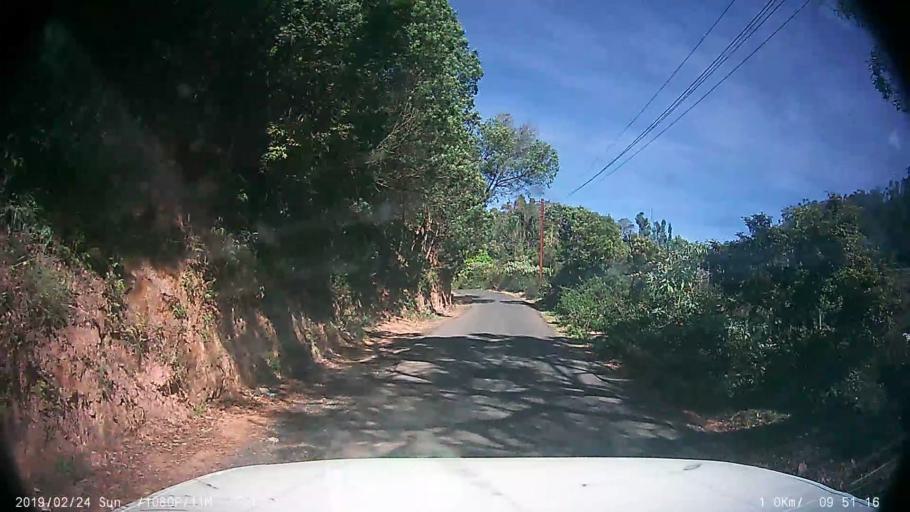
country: IN
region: Tamil Nadu
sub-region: Nilgiri
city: Wellington
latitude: 11.3514
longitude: 76.7753
